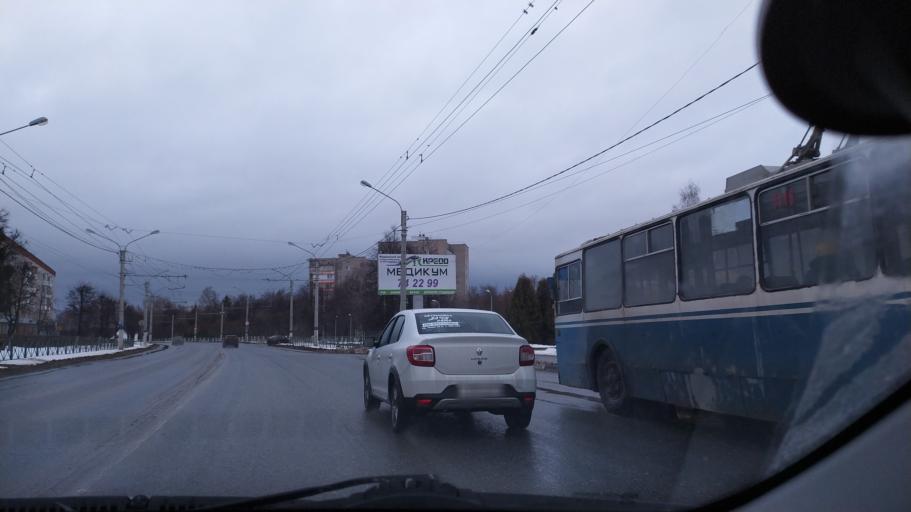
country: RU
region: Chuvashia
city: Novocheboksarsk
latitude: 56.1181
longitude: 47.4926
